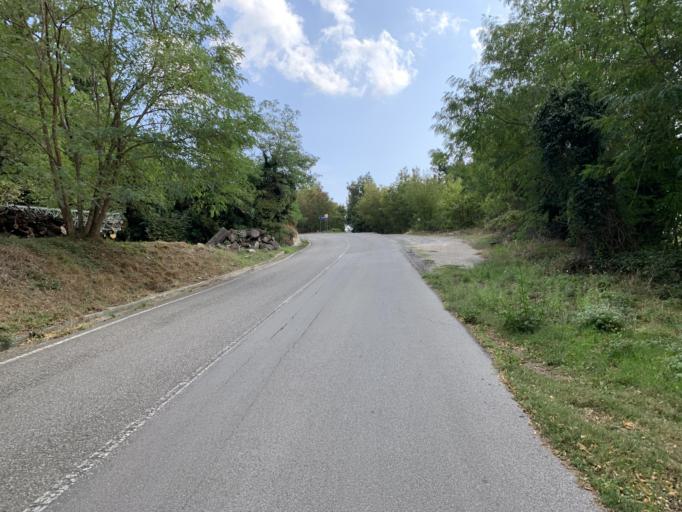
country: IT
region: Liguria
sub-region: Provincia di Savona
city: Orco Feglino
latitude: 44.2213
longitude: 8.3072
